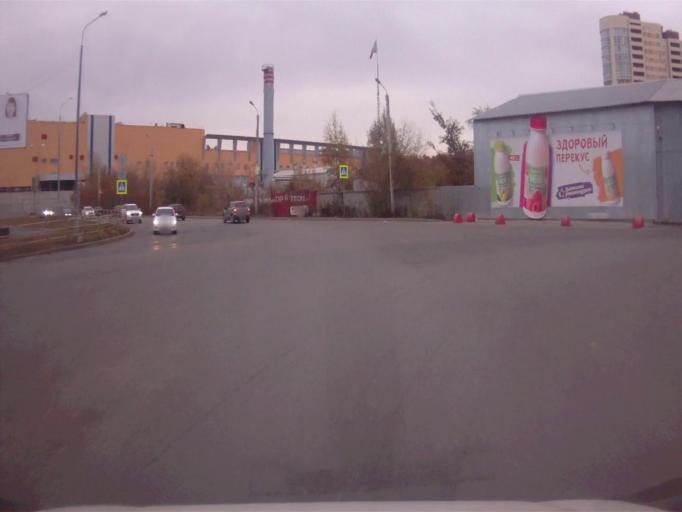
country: RU
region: Chelyabinsk
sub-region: Gorod Chelyabinsk
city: Chelyabinsk
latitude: 55.1716
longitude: 61.3517
